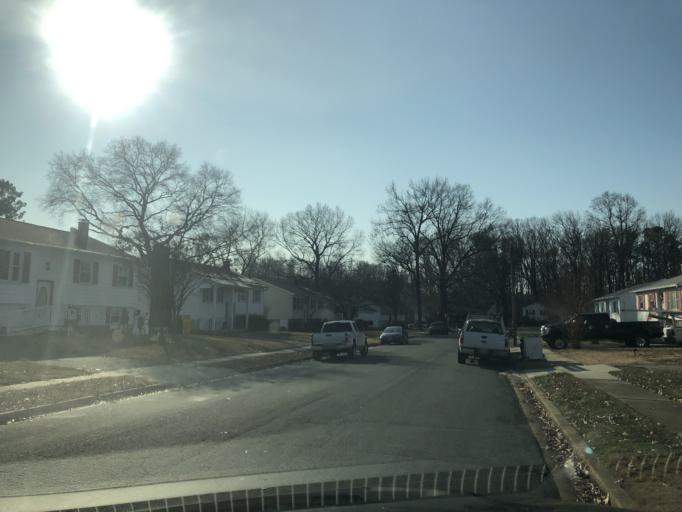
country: US
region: Maryland
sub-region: Anne Arundel County
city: Odenton
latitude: 39.0774
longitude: -76.7042
